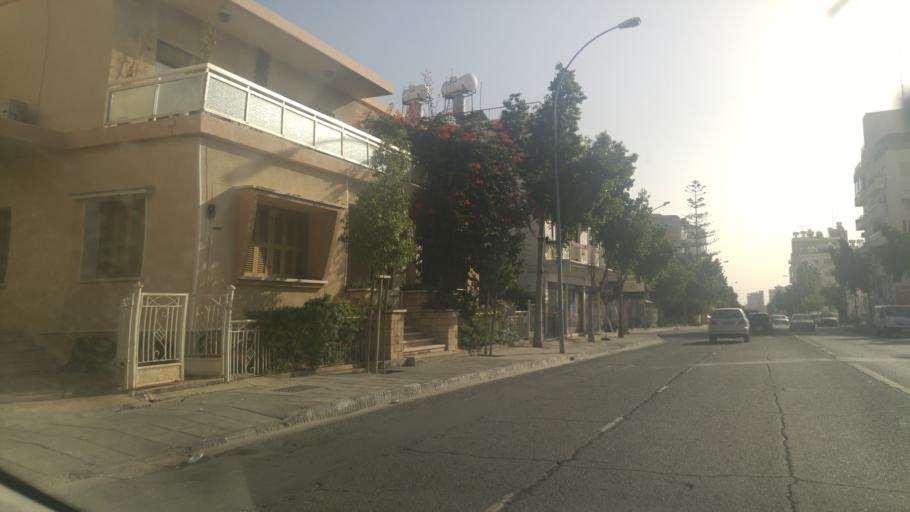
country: CY
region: Limassol
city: Limassol
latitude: 34.6866
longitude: 33.0229
